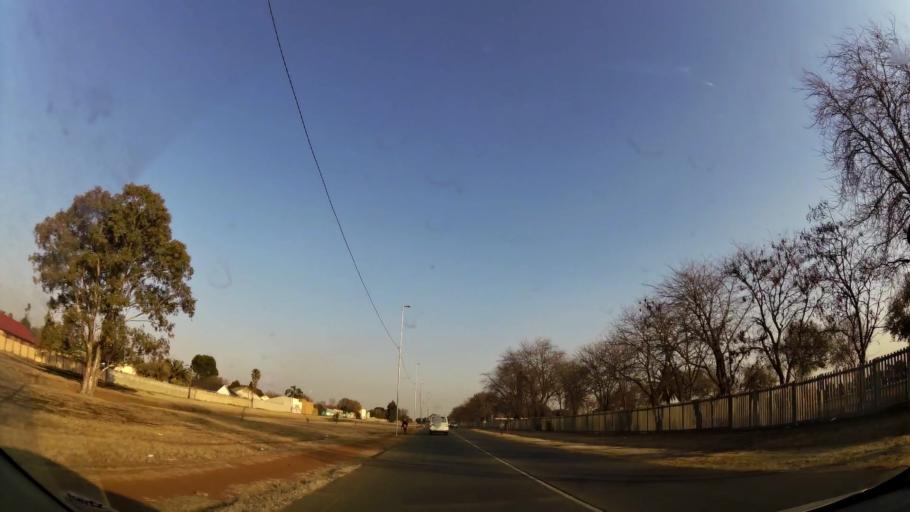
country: ZA
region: Gauteng
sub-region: Ekurhuleni Metropolitan Municipality
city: Germiston
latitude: -26.2762
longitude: 28.2259
